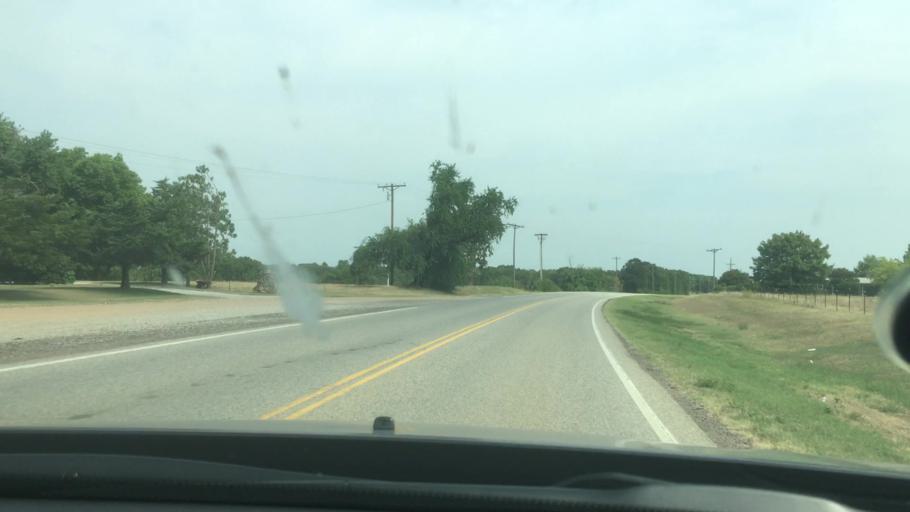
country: US
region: Oklahoma
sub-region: Bryan County
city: Durant
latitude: 34.2008
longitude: -96.4247
